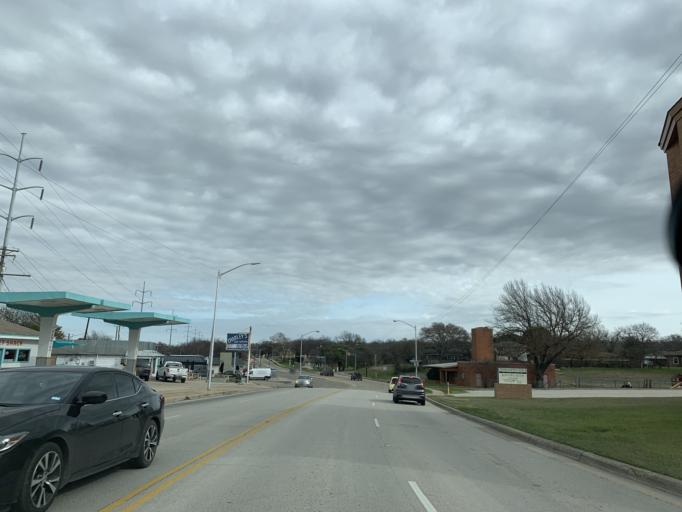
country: US
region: Texas
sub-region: Tarrant County
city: Edgecliff Village
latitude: 32.6804
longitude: -97.3744
